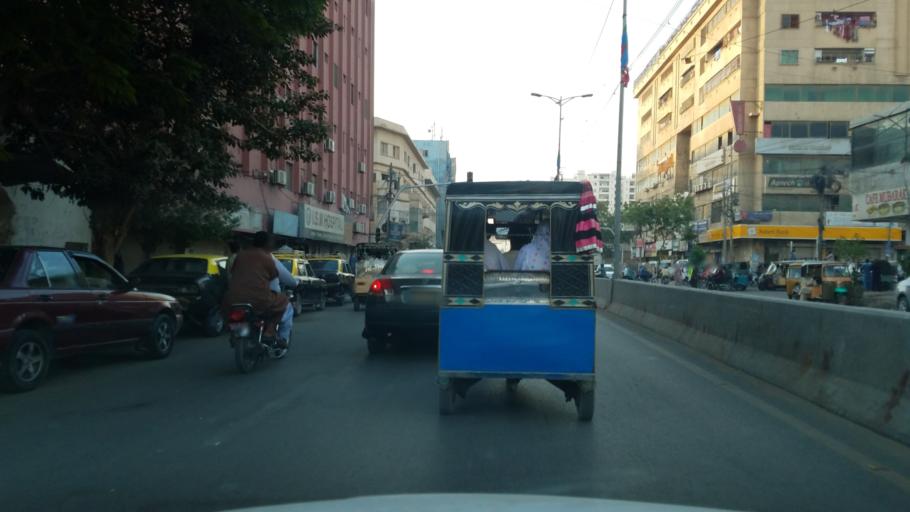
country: PK
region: Sindh
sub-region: Karachi District
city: Karachi
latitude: 24.8664
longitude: 67.0242
